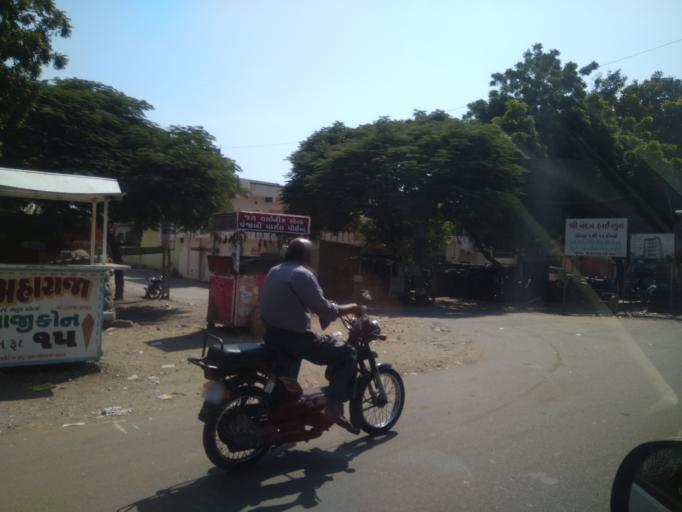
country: IN
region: Gujarat
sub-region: Jamnagar
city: Jamnagar
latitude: 22.4463
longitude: 70.0658
